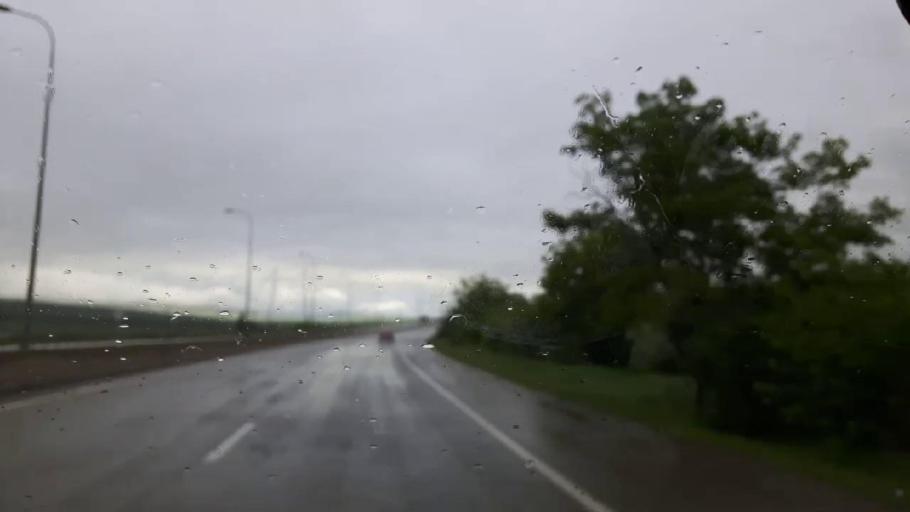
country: GE
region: Shida Kartli
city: Kaspi
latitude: 42.0170
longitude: 44.3174
